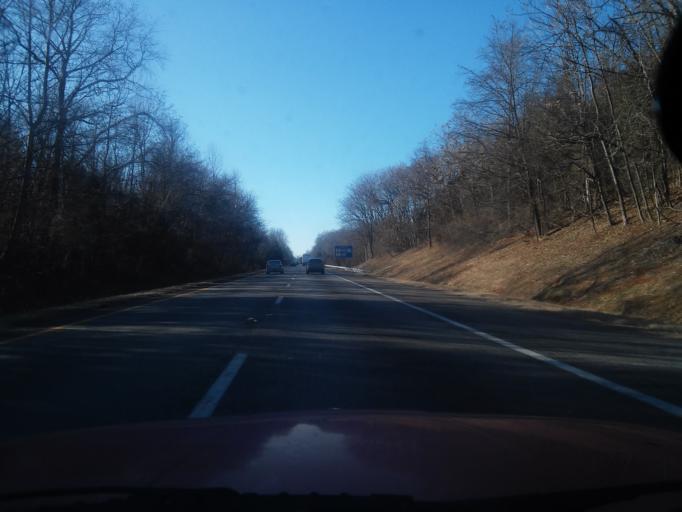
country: US
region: Virginia
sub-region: City of Charlottesville
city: Charlottesville
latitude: 38.0197
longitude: -78.4111
